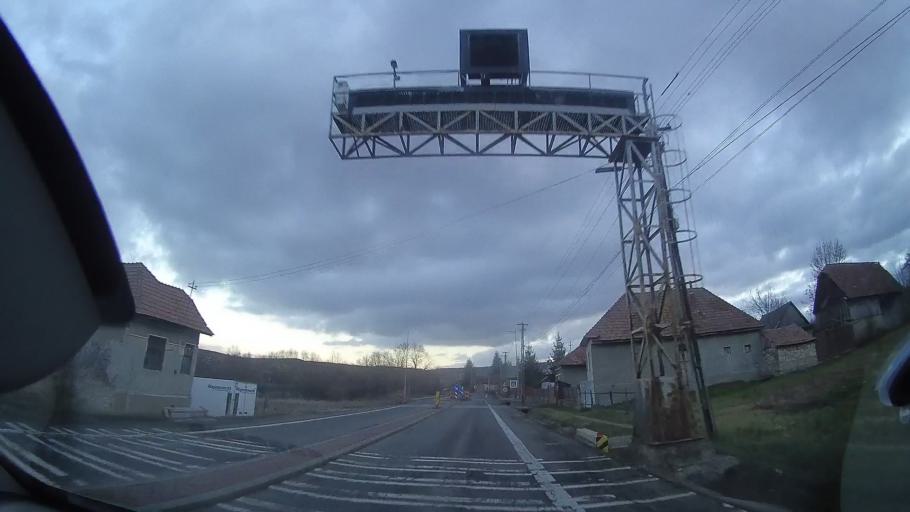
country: RO
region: Cluj
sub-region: Comuna Aghiresu
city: Aghiresu
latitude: 46.8147
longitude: 23.1805
